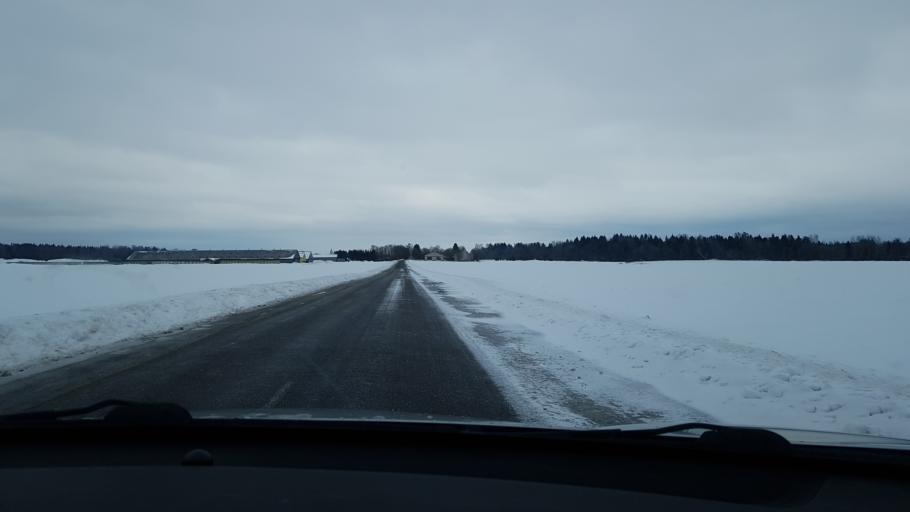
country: EE
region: Jaervamaa
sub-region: Koeru vald
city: Koeru
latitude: 58.9789
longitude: 25.9964
